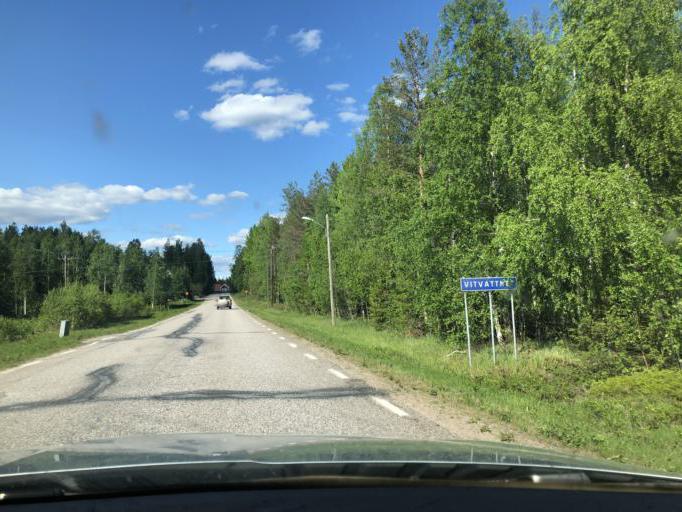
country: SE
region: Norrbotten
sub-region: Kalix Kommun
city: Kalix
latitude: 66.0562
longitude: 23.1928
